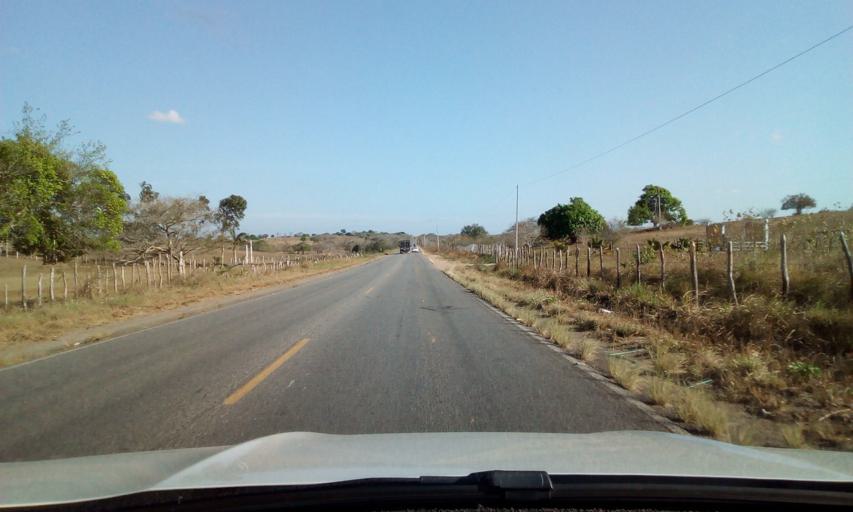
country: BR
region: Paraiba
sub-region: Mulungu
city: Mulungu
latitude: -6.9346
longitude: -35.4342
